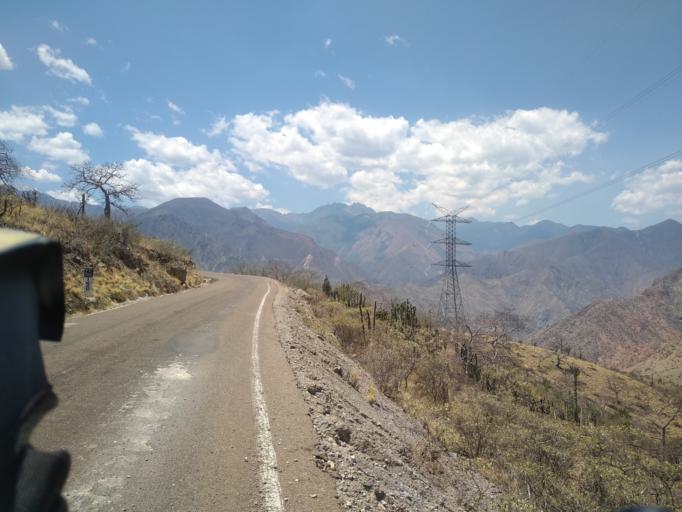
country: PE
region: Amazonas
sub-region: Provincia de Chachapoyas
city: Balsas
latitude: -6.8487
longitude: -78.0361
